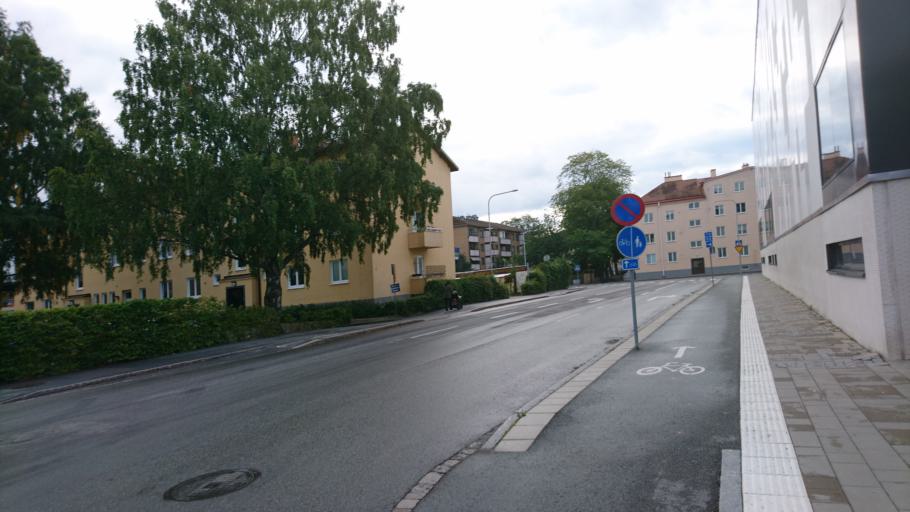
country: SE
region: Uppsala
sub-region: Uppsala Kommun
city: Uppsala
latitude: 59.8706
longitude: 17.6258
